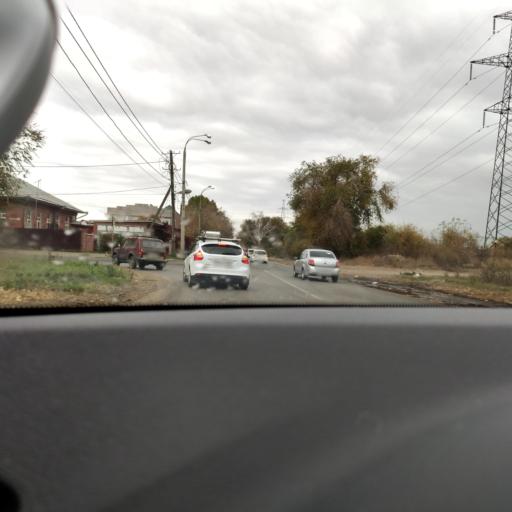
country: RU
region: Samara
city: Smyshlyayevka
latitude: 53.2300
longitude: 50.3086
